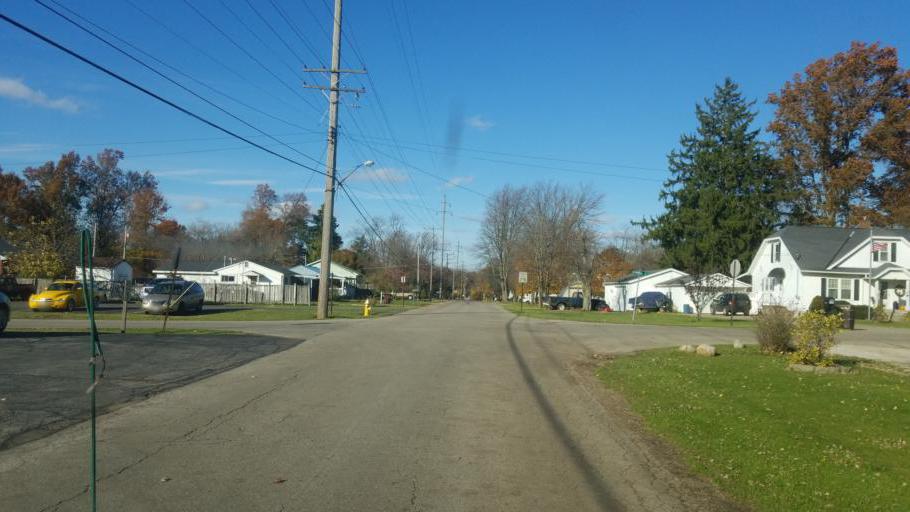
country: US
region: Ohio
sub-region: Richland County
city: Ontario
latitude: 40.7797
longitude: -82.5558
